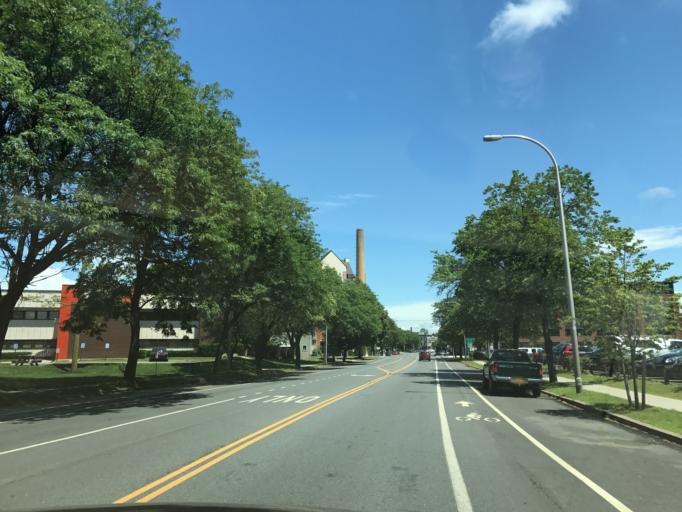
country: US
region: New York
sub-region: Warren County
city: Glens Falls
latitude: 43.3071
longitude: -73.6479
